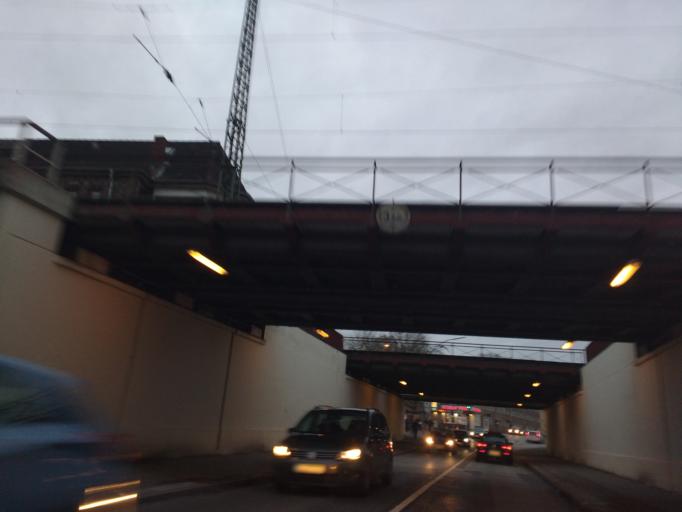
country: DE
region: Hamburg
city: Eidelstedt
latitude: 53.6030
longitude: 9.8916
